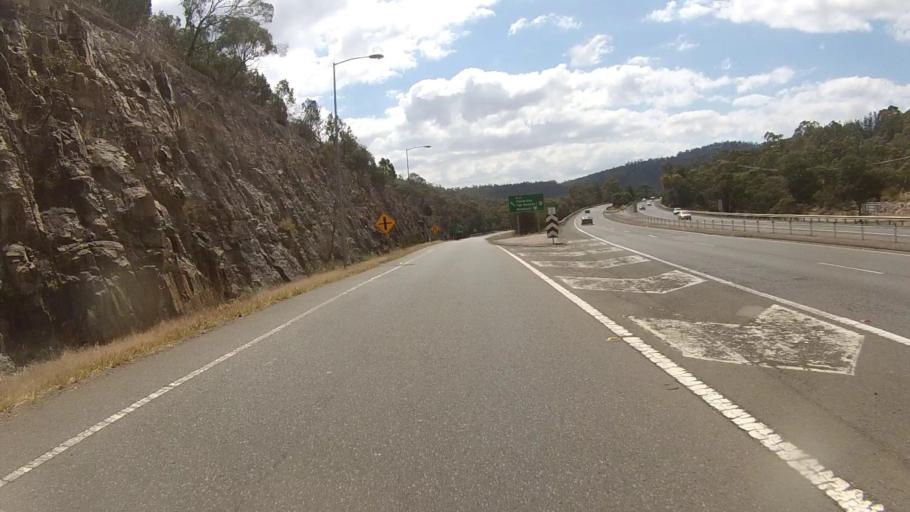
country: AU
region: Tasmania
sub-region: Clarence
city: Cambridge
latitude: -42.8472
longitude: 147.4195
